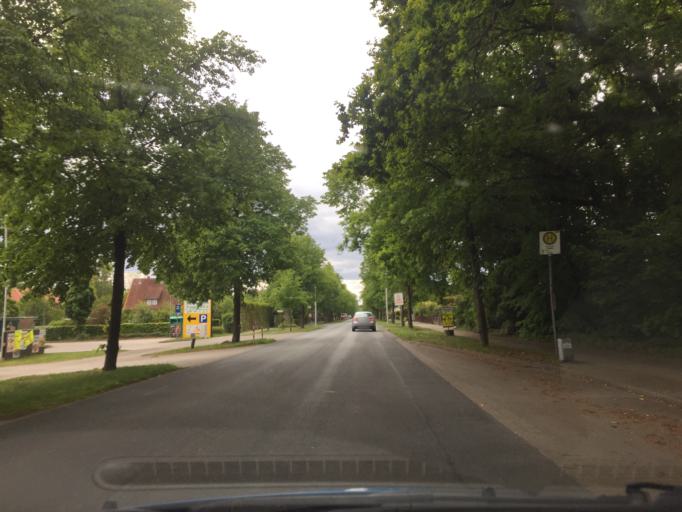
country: DE
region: Lower Saxony
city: Uelzen
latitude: 52.9264
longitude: 10.5280
